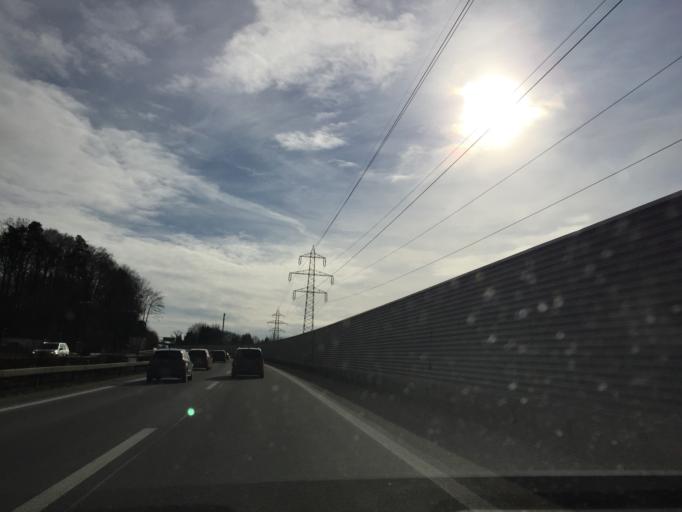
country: CH
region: Zurich
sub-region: Bezirk Horgen
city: Kilchberg / Baechler-Stocken
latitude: 47.3212
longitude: 8.5333
